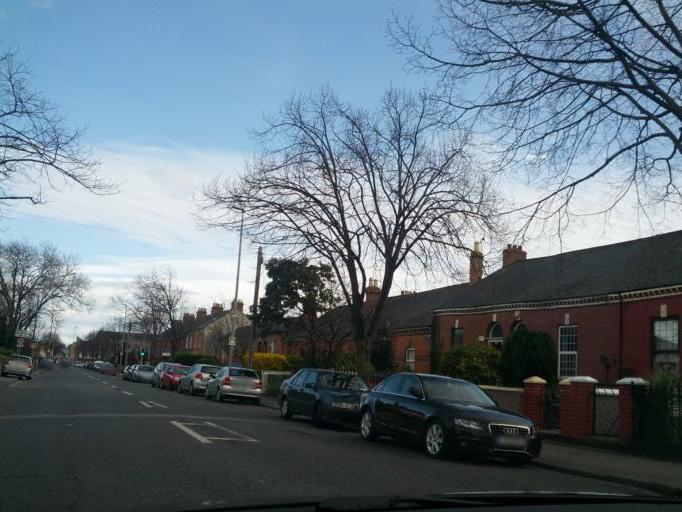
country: IE
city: Fairview
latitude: 53.3620
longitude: -6.2476
